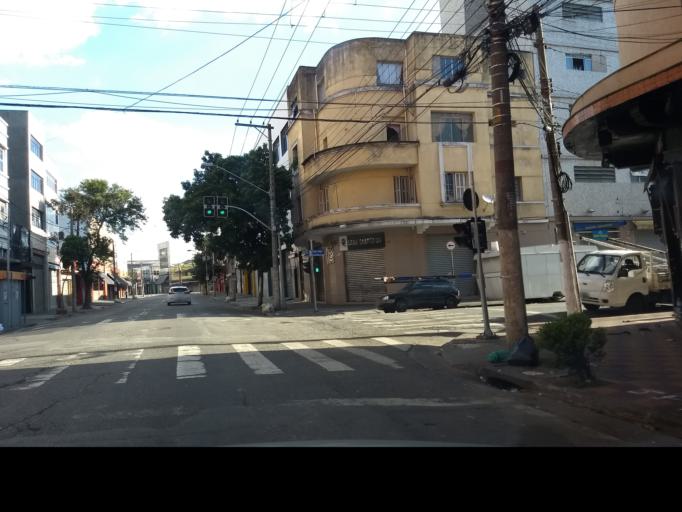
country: BR
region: Sao Paulo
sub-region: Sao Paulo
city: Sao Paulo
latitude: -23.5338
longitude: -46.6220
